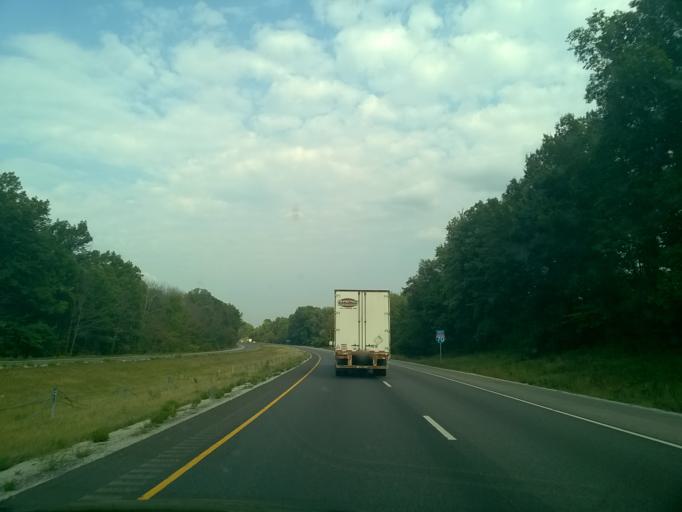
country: US
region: Indiana
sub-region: Clay County
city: Brazil
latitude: 39.4490
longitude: -87.1167
